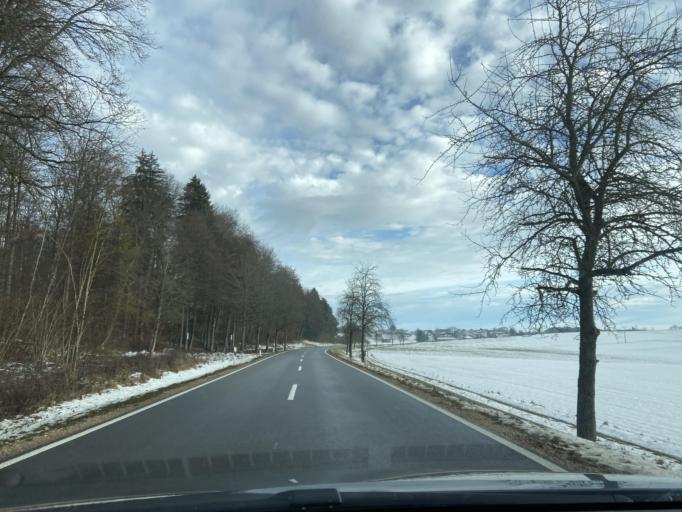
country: DE
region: Baden-Wuerttemberg
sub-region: Tuebingen Region
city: Hettingen
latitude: 48.2424
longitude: 9.2963
